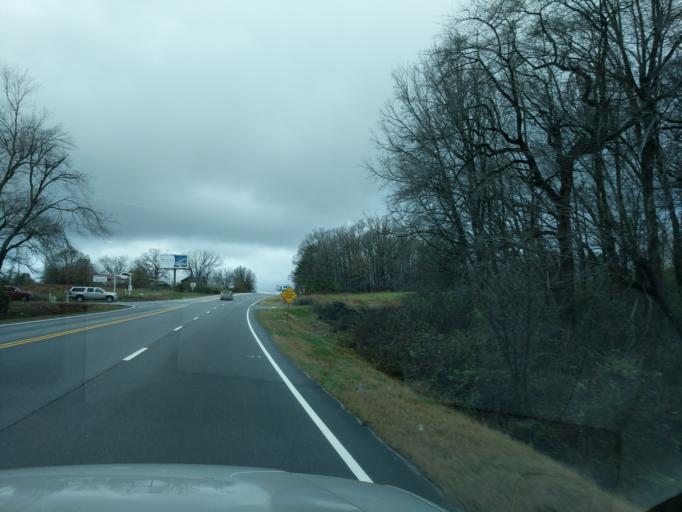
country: US
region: Georgia
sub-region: Franklin County
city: Lavonia
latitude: 34.3920
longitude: -83.1019
